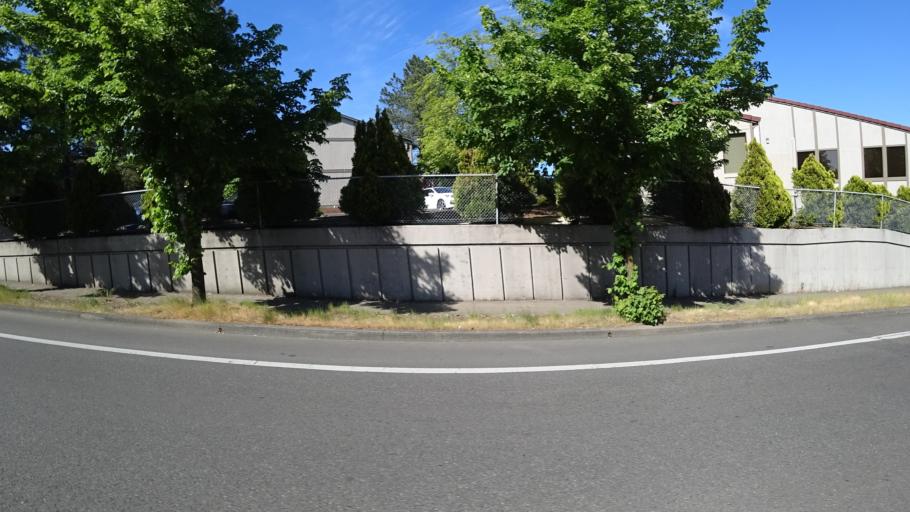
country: US
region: Oregon
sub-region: Washington County
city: Beaverton
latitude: 45.4621
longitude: -122.7990
